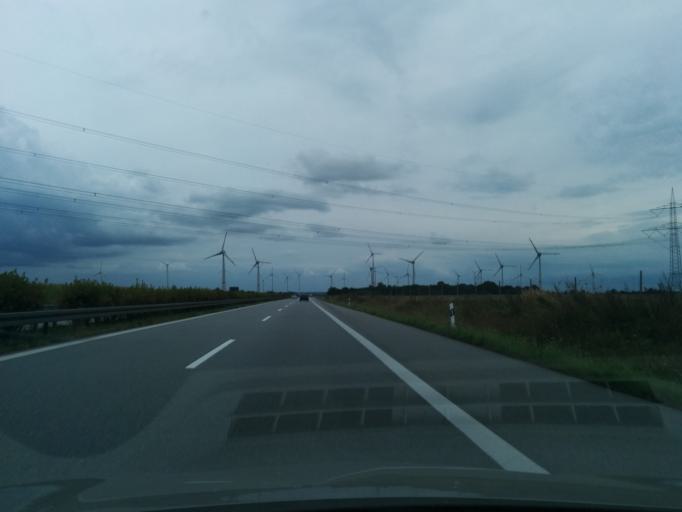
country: DE
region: Mecklenburg-Vorpommern
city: Kessin
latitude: 53.7480
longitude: 13.3340
